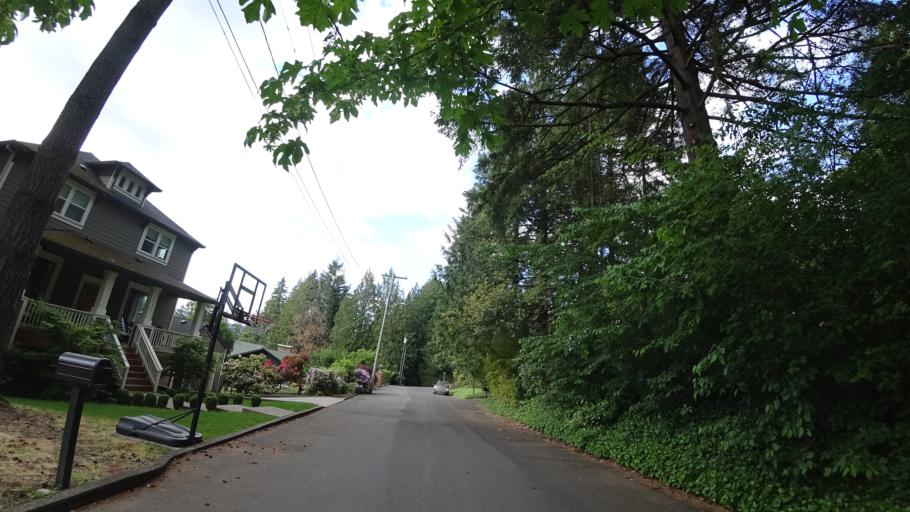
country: US
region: Oregon
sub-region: Washington County
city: Garden Home-Whitford
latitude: 45.4705
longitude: -122.7260
